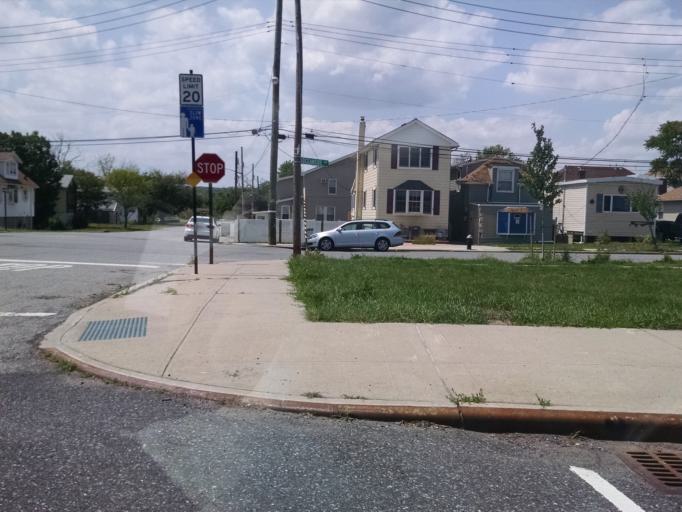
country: US
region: New York
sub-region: Richmond County
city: Staten Island
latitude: 40.5781
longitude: -74.0793
